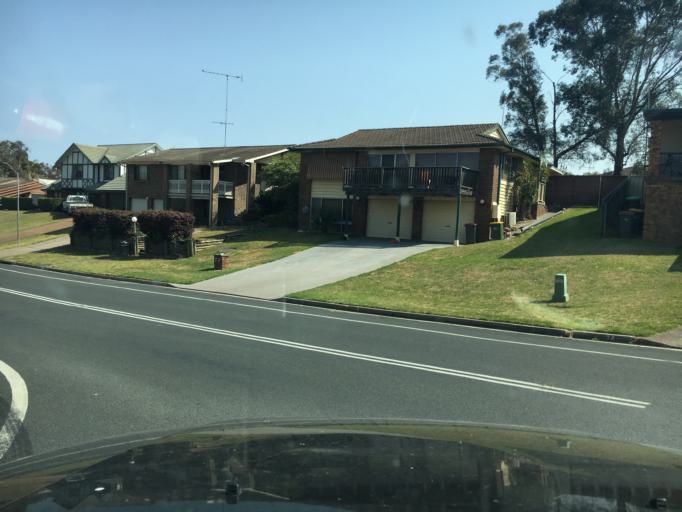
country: AU
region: New South Wales
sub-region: Singleton
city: Singleton
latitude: -32.5583
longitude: 151.1597
